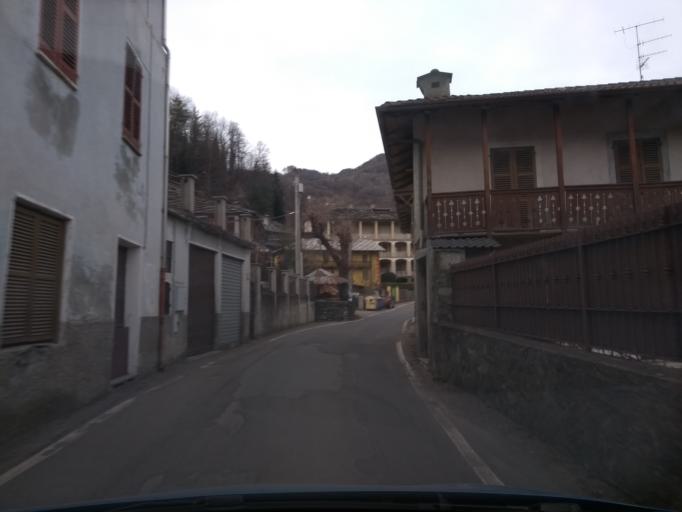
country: IT
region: Piedmont
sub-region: Provincia di Torino
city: Viu
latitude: 45.2346
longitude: 7.3718
